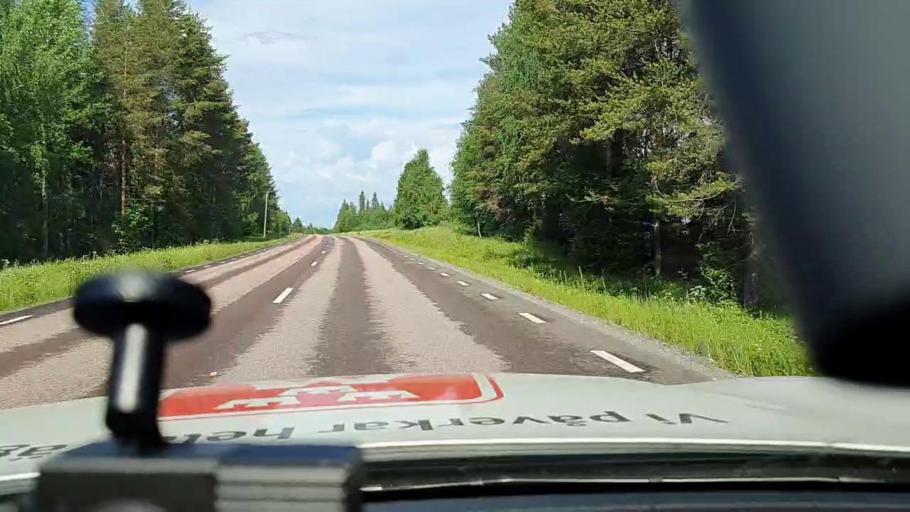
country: SE
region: Norrbotten
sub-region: Alvsbyns Kommun
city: AElvsbyn
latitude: 66.0224
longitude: 21.1285
